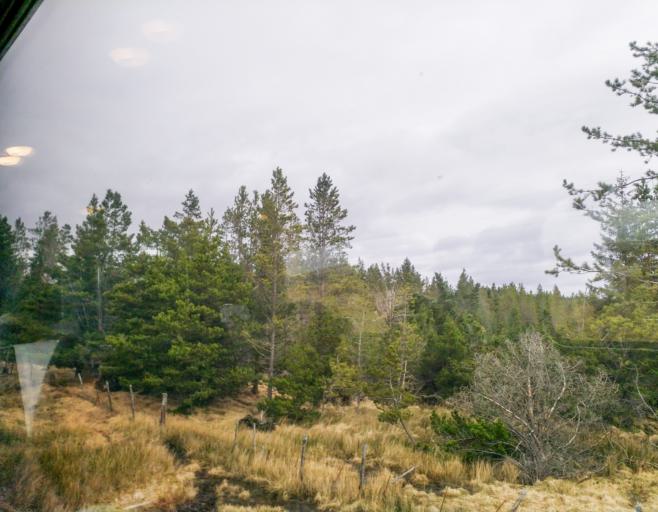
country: GB
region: Scotland
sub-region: Highland
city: Spean Bridge
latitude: 56.6546
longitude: -4.5654
